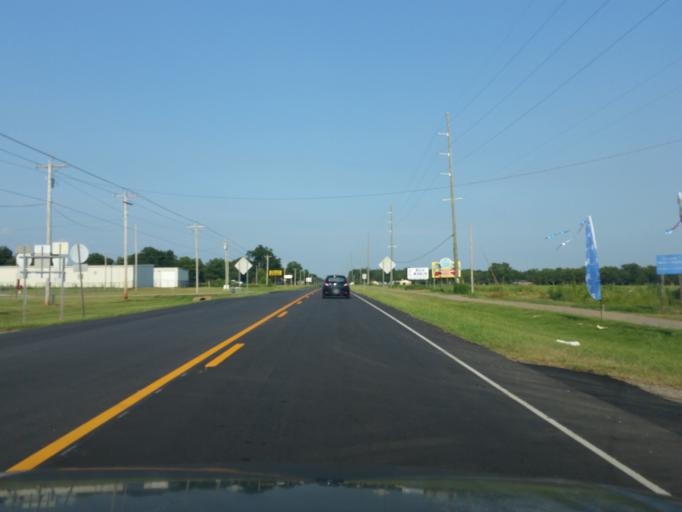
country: US
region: Alabama
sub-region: Baldwin County
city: Point Clear
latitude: 30.4212
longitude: -87.8854
